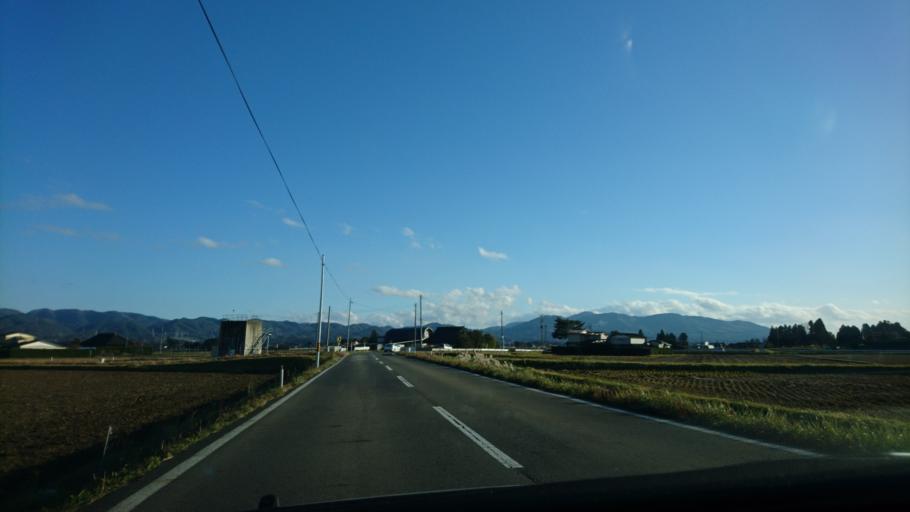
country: JP
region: Iwate
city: Mizusawa
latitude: 39.1000
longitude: 141.1581
